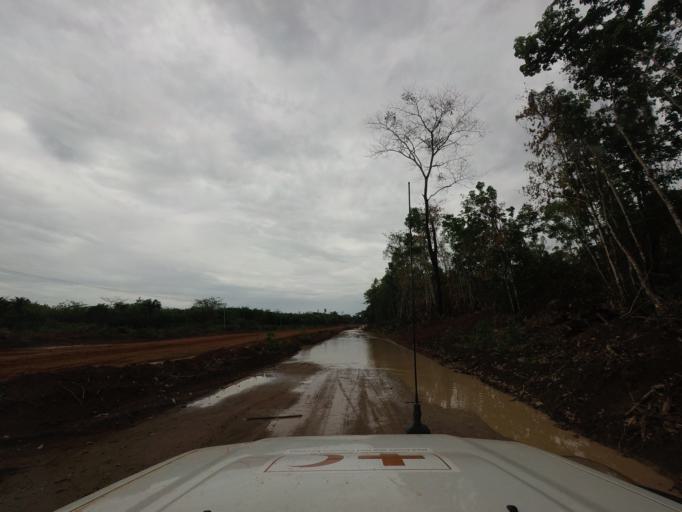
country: LR
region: Nimba
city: Sanniquellie
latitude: 7.2498
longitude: -8.8595
